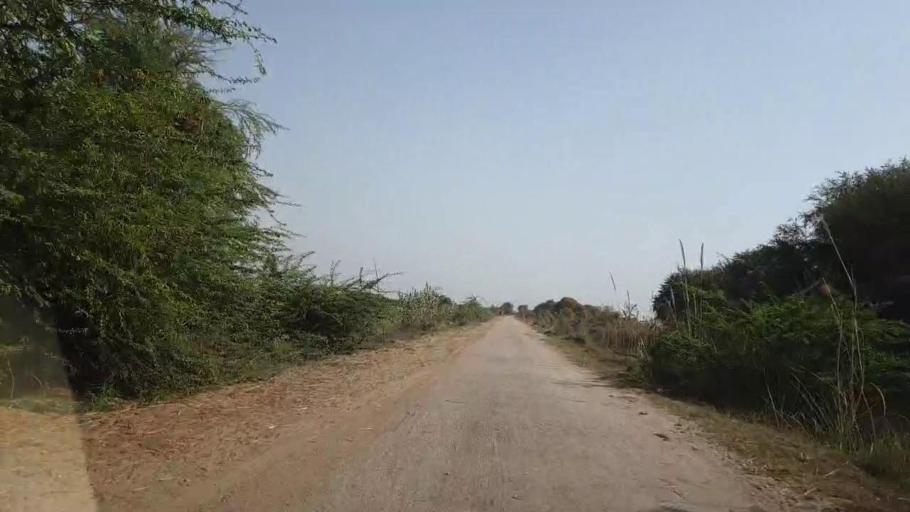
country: PK
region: Sindh
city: Rajo Khanani
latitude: 25.0538
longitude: 68.8330
